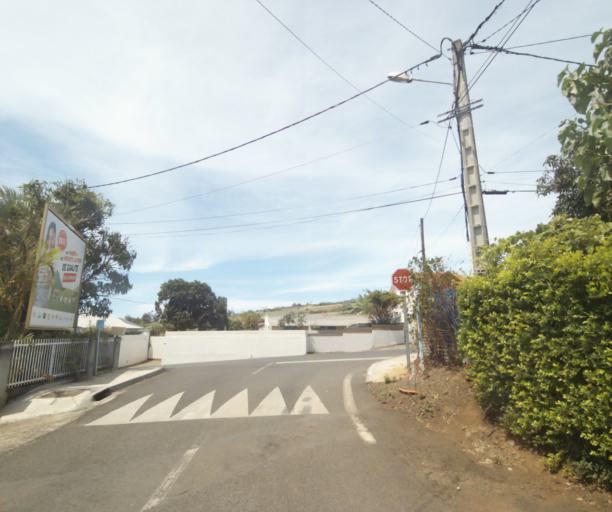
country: RE
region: Reunion
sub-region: Reunion
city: Saint-Paul
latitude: -21.0439
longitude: 55.2834
